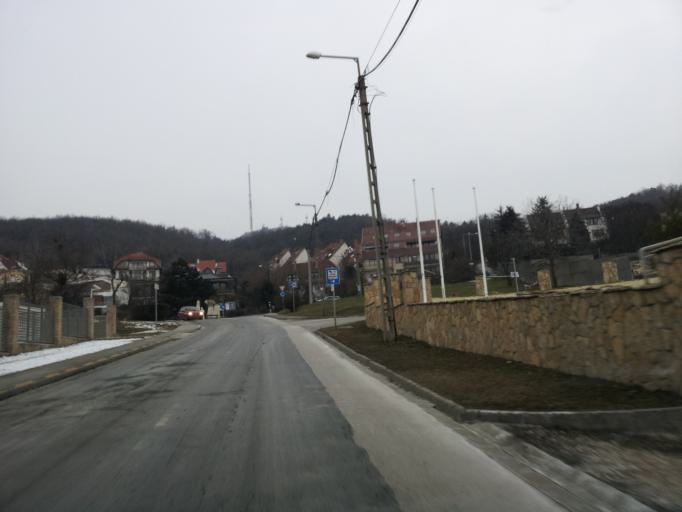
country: HU
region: Budapest
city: Budapest XII. keruelet
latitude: 47.4871
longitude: 18.9908
